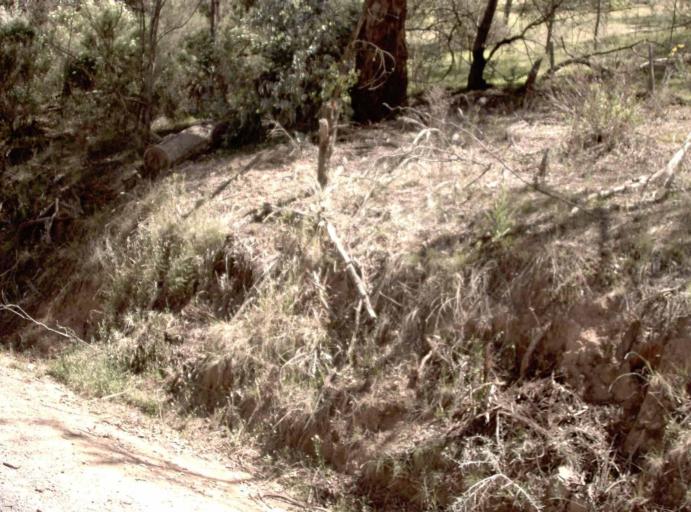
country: AU
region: New South Wales
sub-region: Bombala
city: Bombala
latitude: -37.1084
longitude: 148.6408
